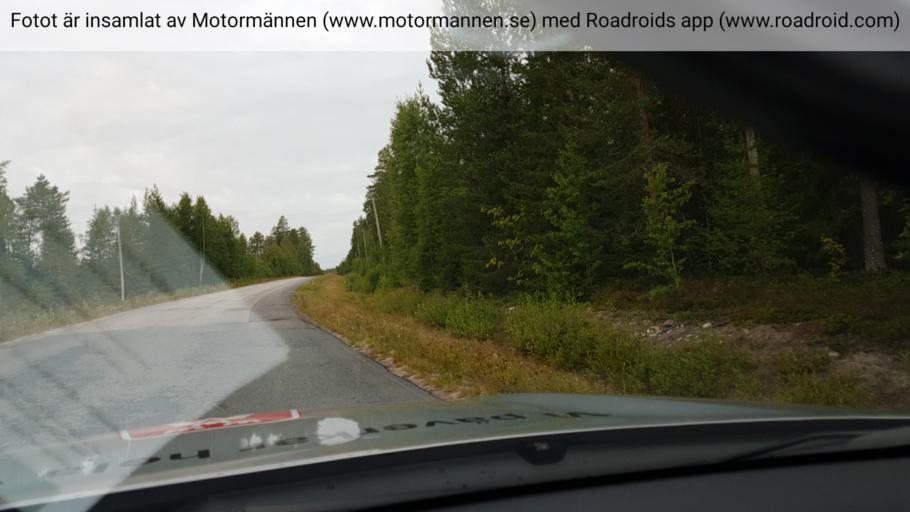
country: SE
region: Norrbotten
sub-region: Bodens Kommun
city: Saevast
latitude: 65.6671
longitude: 21.7490
